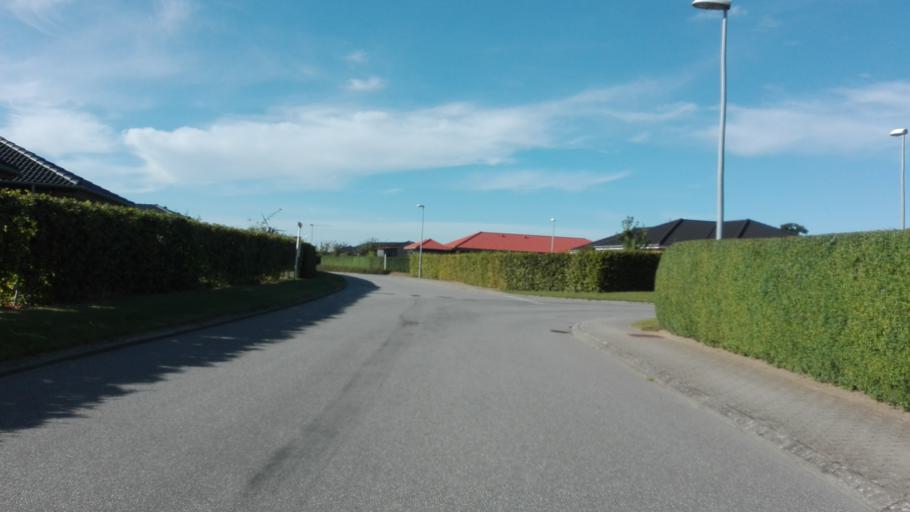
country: DK
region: South Denmark
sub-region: Fredericia Kommune
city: Fredericia
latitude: 55.5803
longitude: 9.7052
